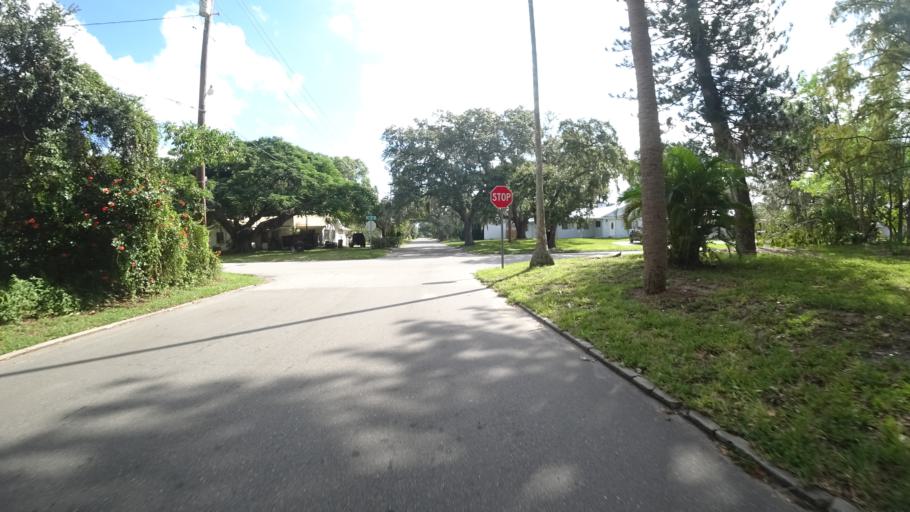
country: US
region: Florida
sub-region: Manatee County
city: West Bradenton
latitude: 27.4976
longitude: -82.6082
